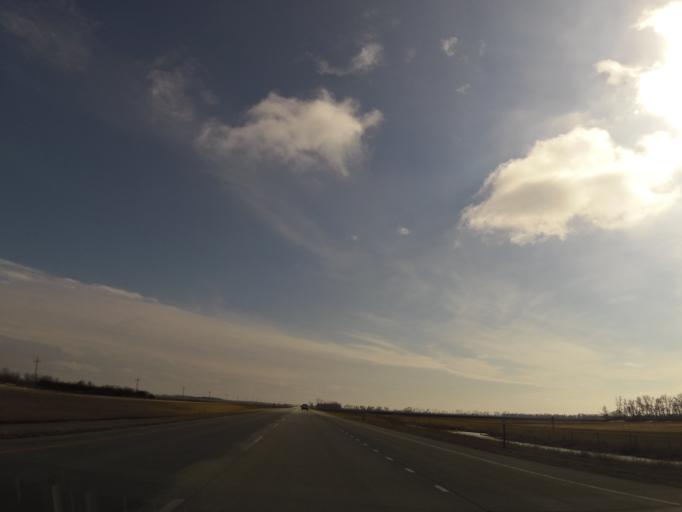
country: US
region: North Dakota
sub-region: Walsh County
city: Grafton
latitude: 48.2913
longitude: -97.1893
